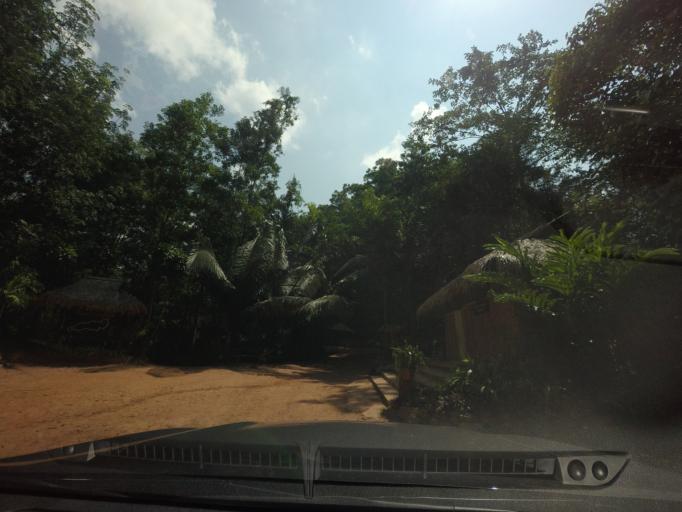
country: TH
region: Nan
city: Bo Kluea
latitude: 19.0157
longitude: 101.2102
